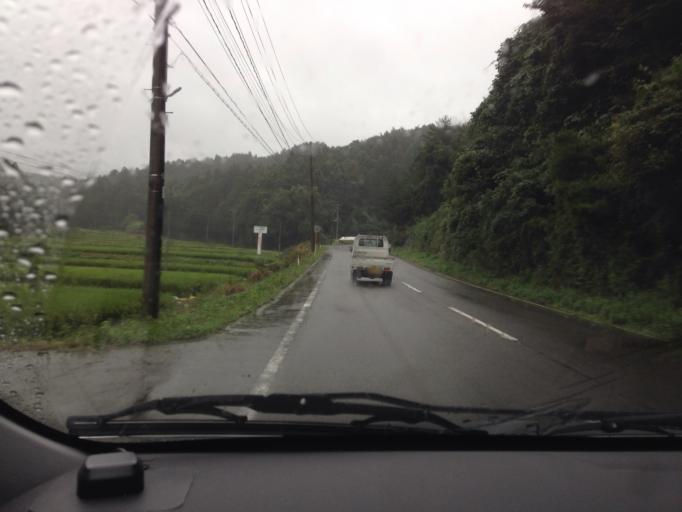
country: JP
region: Fukushima
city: Koriyama
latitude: 37.4367
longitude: 140.2631
